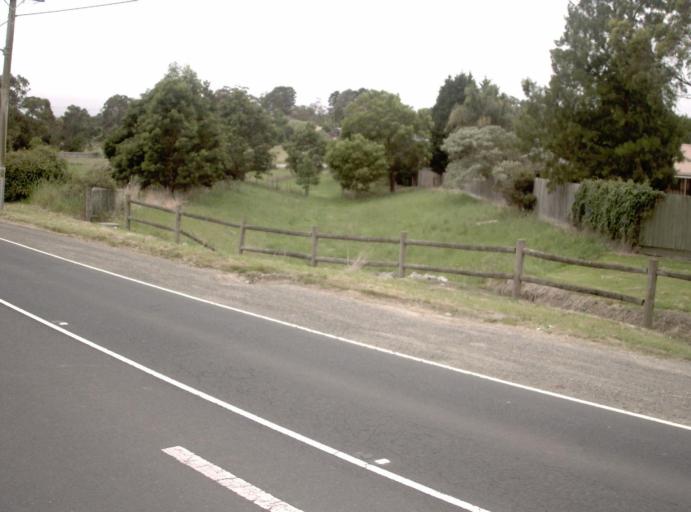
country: AU
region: Victoria
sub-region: Casey
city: Endeavour Hills
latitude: -37.9807
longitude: 145.2782
